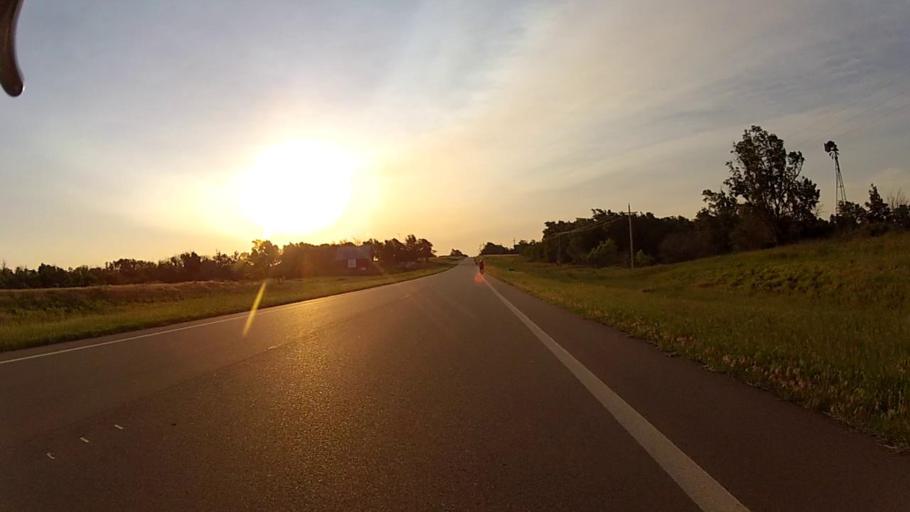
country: US
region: Kansas
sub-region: Harper County
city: Anthony
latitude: 37.1525
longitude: -97.9599
